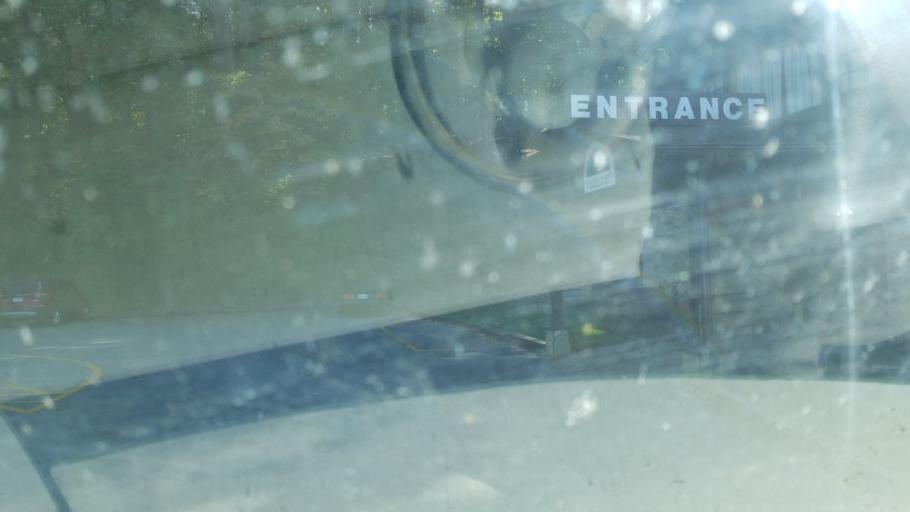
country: US
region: Virginia
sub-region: Warren County
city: Front Royal
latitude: 38.8996
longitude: -78.2160
